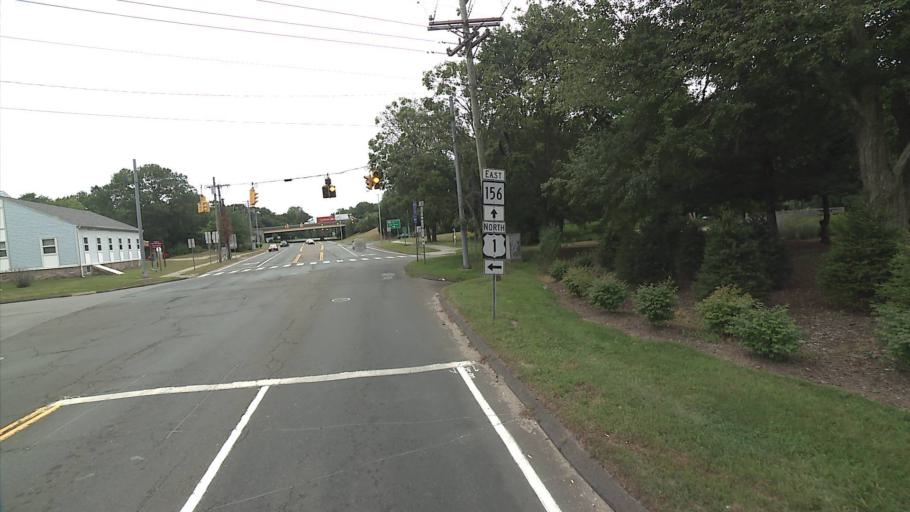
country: US
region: Connecticut
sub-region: Middlesex County
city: Old Saybrook Center
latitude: 41.3224
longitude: -72.3404
